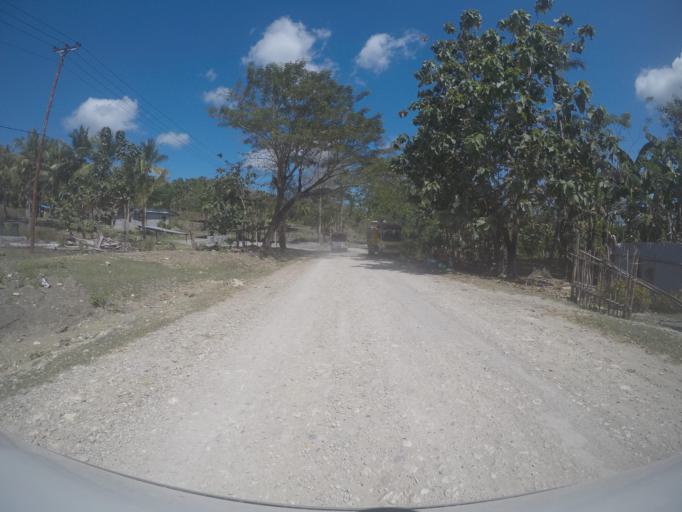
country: TL
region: Viqueque
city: Viqueque
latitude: -8.9144
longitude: 126.3972
